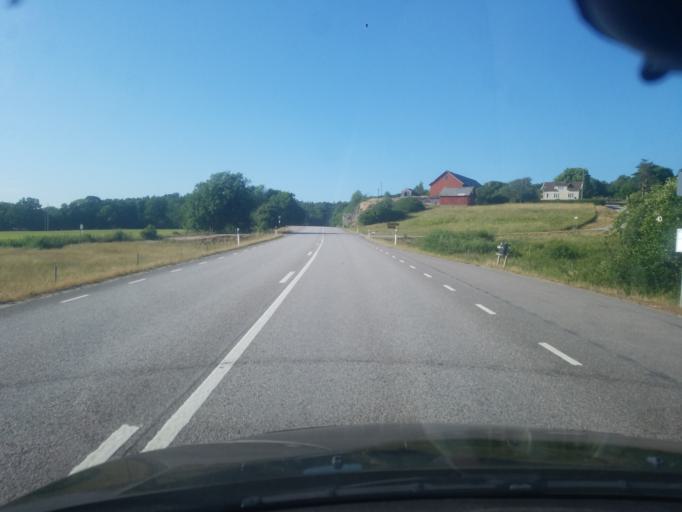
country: SE
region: Vaestra Goetaland
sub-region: Orust
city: Henan
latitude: 58.2739
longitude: 11.6939
